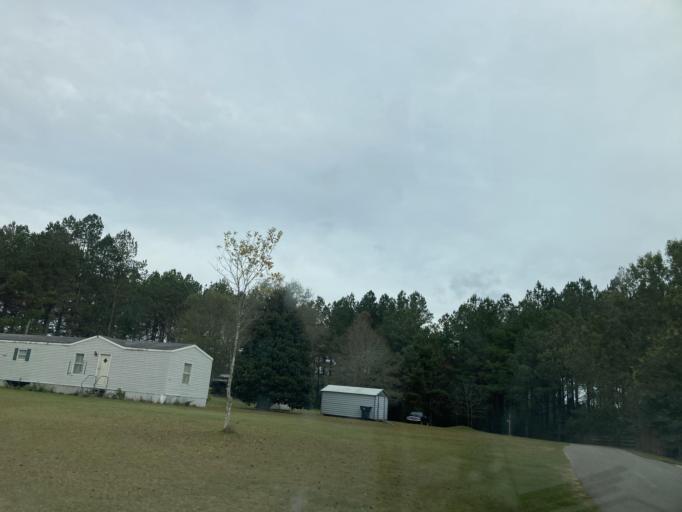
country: US
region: Mississippi
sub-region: Lamar County
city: Purvis
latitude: 31.1589
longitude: -89.4567
